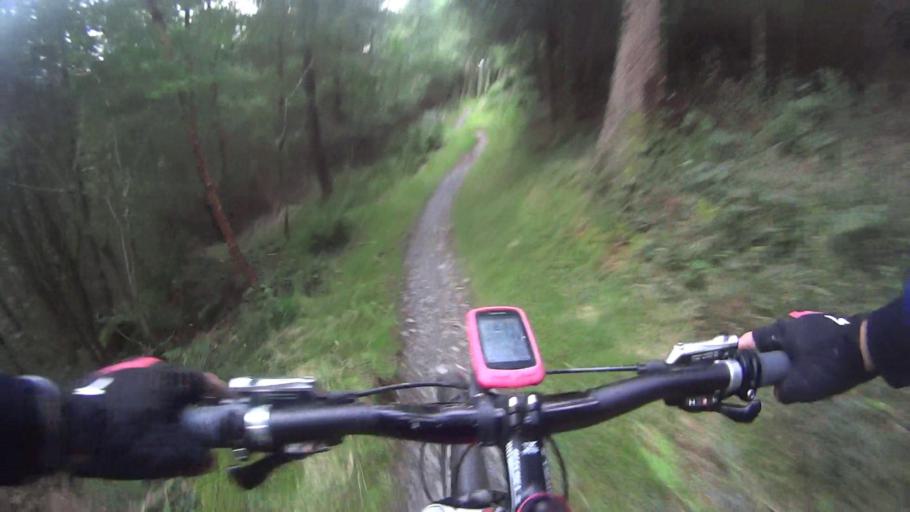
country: GB
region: Wales
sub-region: County of Ceredigion
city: Bow Street
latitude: 52.4196
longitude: -3.9132
